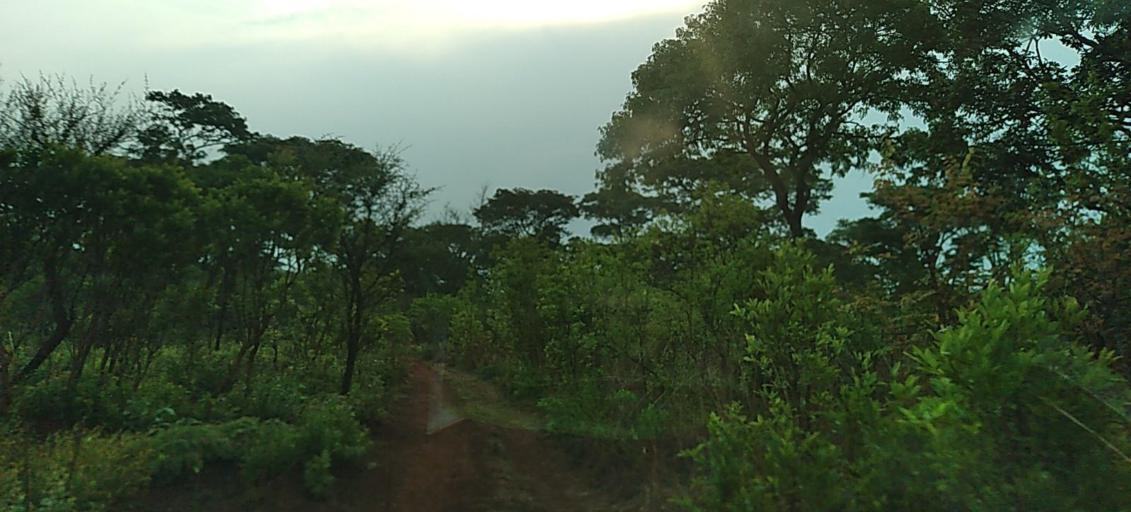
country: ZM
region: North-Western
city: Solwezi
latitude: -12.0440
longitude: 26.0241
